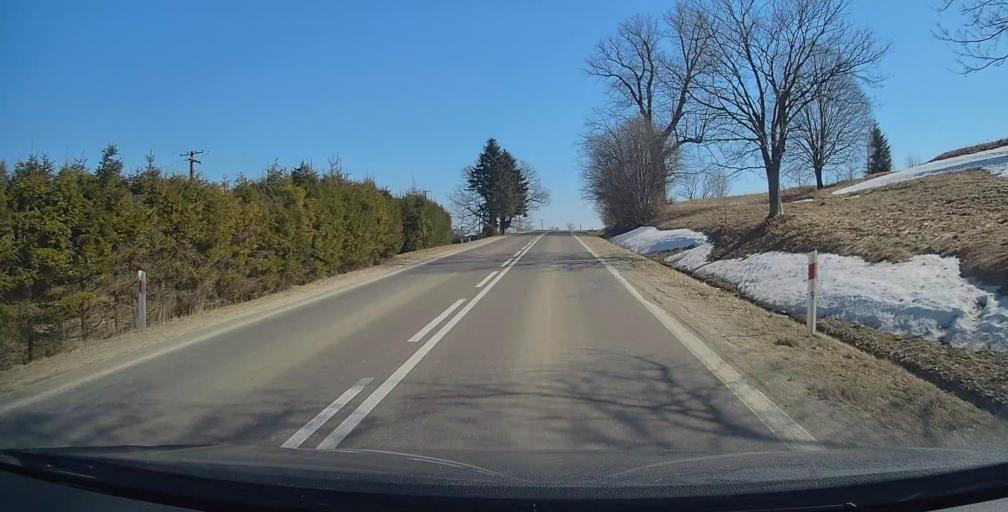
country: PL
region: Subcarpathian Voivodeship
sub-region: Powiat sanocki
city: Tyrawa Woloska
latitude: 49.6114
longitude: 22.4389
